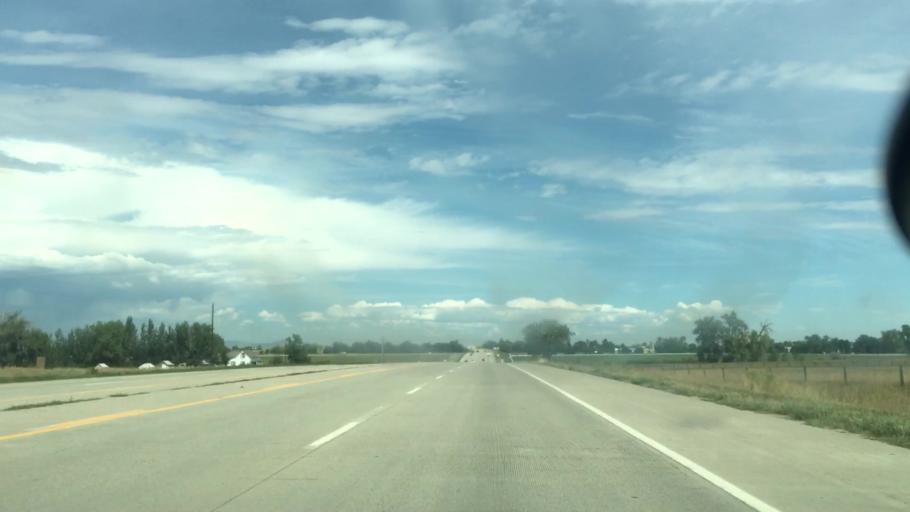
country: US
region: Colorado
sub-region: Boulder County
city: Longmont
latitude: 40.2233
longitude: -105.1023
